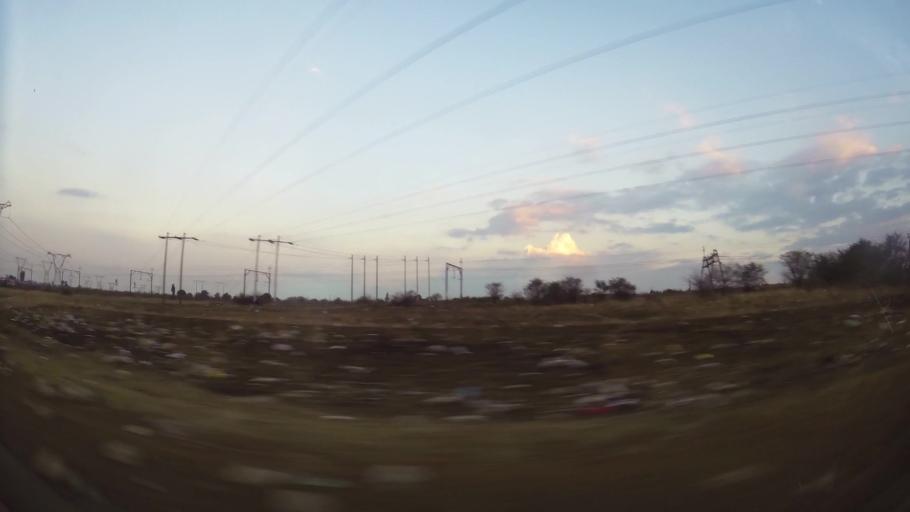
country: ZA
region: Gauteng
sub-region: City of Johannesburg Metropolitan Municipality
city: Orange Farm
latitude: -26.5612
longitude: 27.8732
